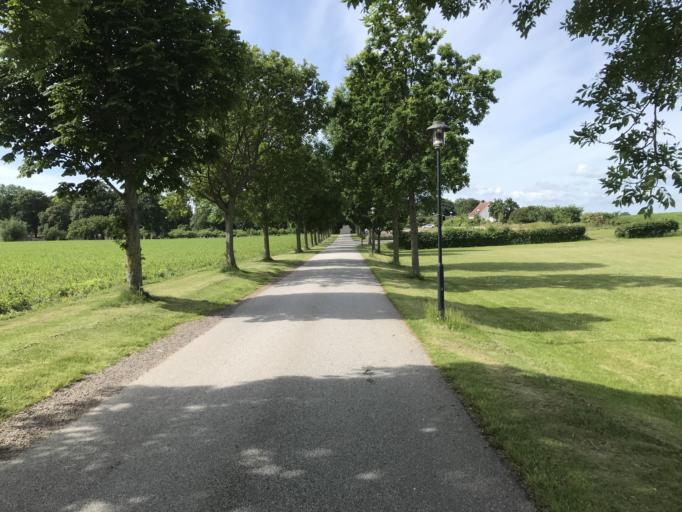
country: SE
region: Skane
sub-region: Helsingborg
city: Rydeback
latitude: 55.9431
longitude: 12.7821
